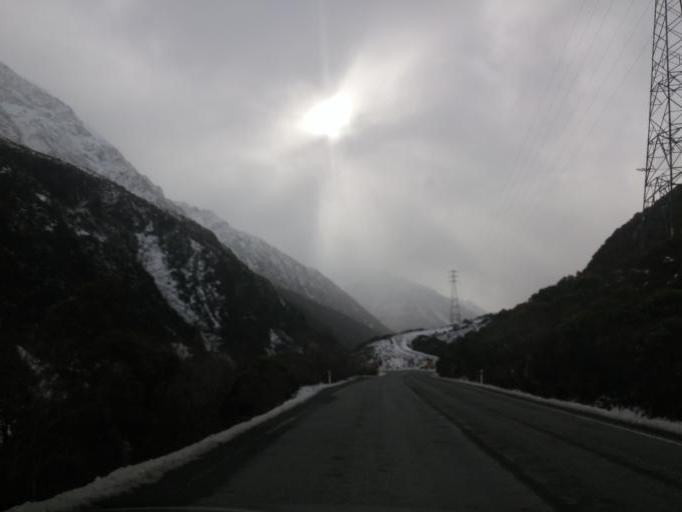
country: NZ
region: West Coast
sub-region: Grey District
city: Greymouth
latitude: -42.8922
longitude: 171.5575
